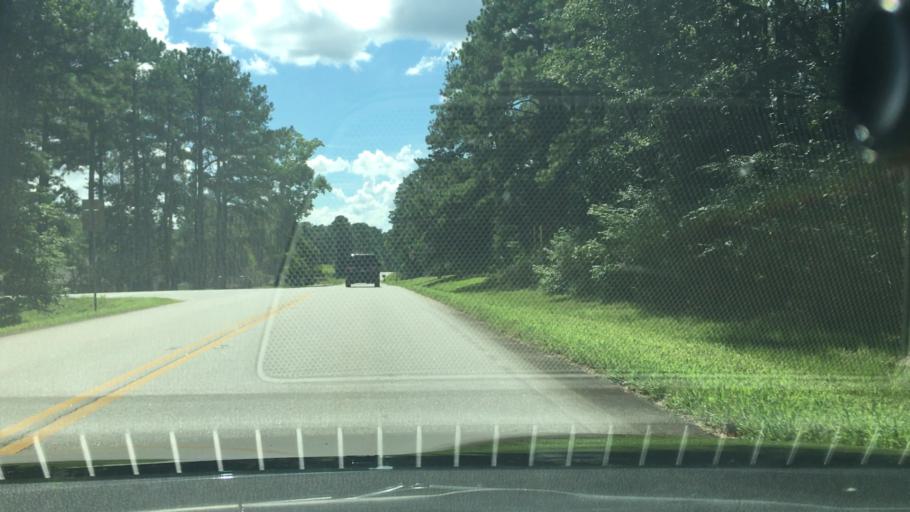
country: US
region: Georgia
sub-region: Jasper County
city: Monticello
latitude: 33.3025
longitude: -83.6338
